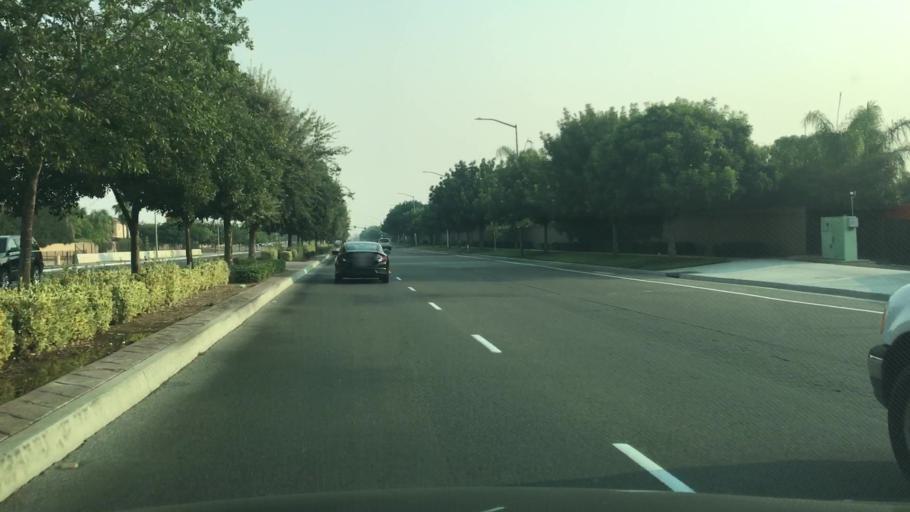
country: US
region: California
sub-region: Fresno County
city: Clovis
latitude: 36.8563
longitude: -119.7298
